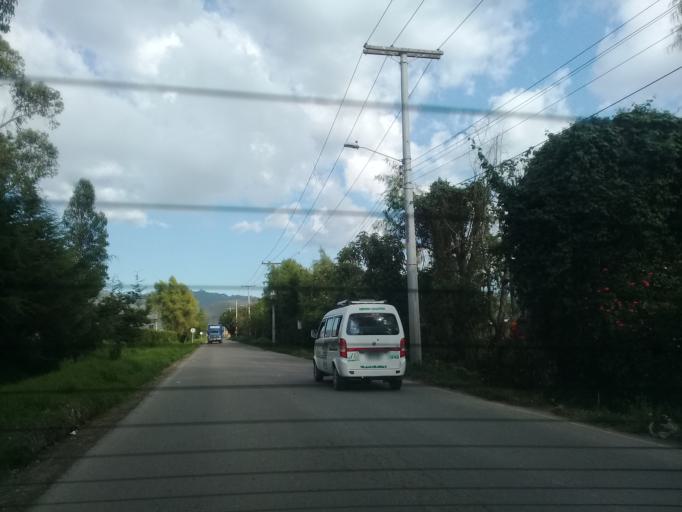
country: CO
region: Cundinamarca
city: El Rosal
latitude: 4.8189
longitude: -74.2322
